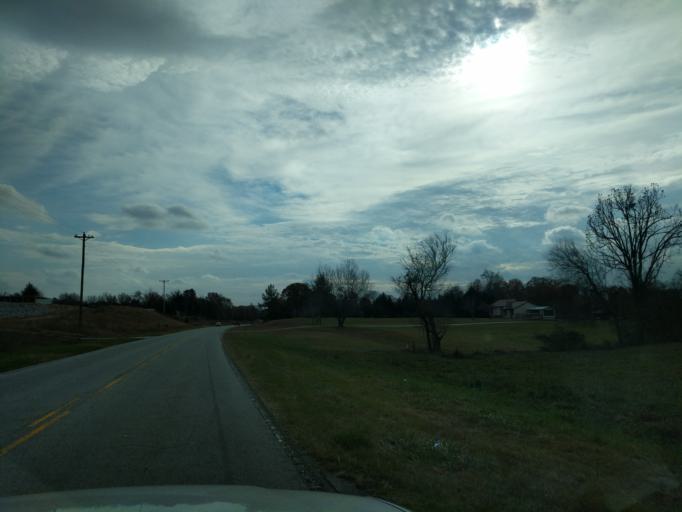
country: US
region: South Carolina
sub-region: Oconee County
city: Westminster
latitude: 34.5953
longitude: -83.0454
